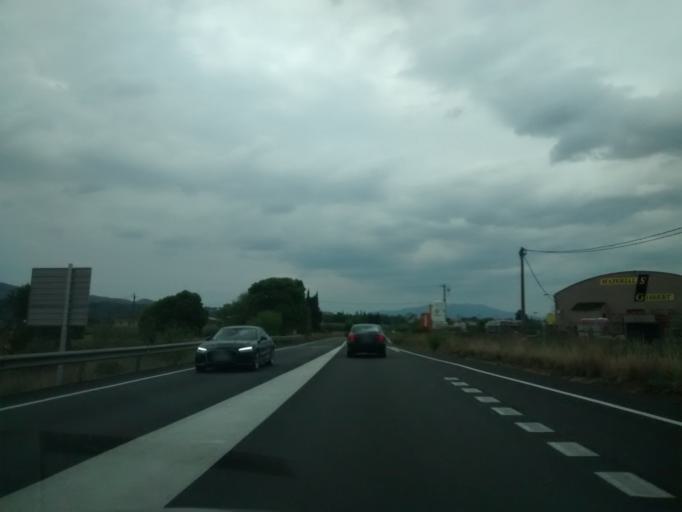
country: ES
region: Catalonia
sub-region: Provincia de Tarragona
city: Tortosa
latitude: 40.8373
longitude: 0.5141
